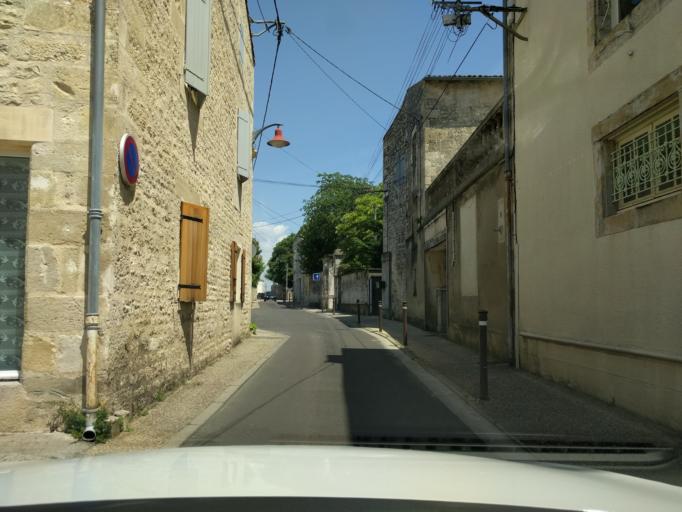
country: FR
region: Poitou-Charentes
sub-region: Departement des Deux-Sevres
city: Niort
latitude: 46.3481
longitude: -0.4706
